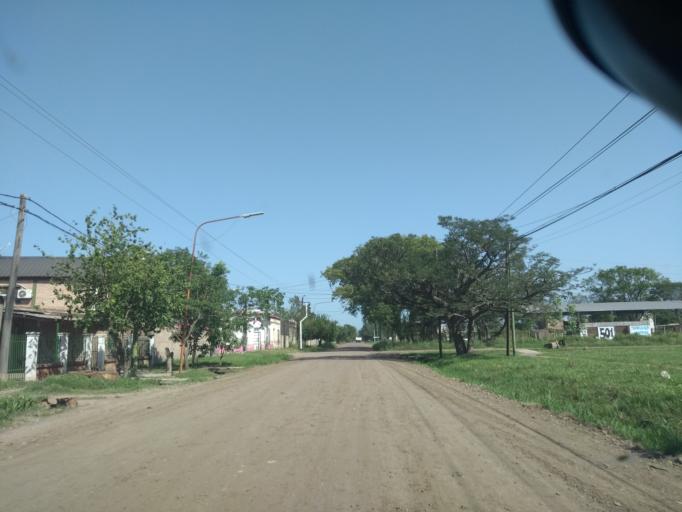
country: AR
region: Chaco
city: Fontana
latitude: -27.4167
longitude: -59.0398
